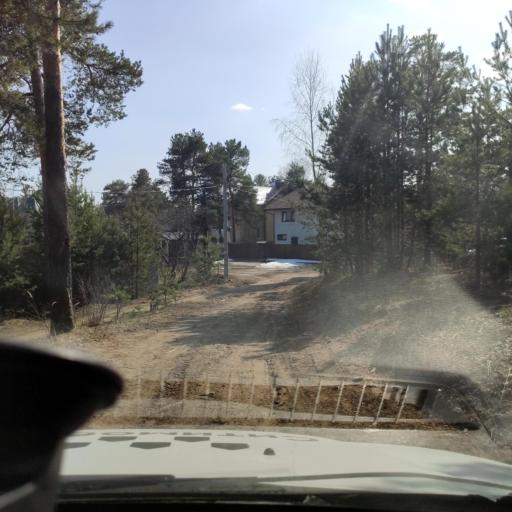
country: RU
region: Perm
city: Perm
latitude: 58.0554
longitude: 56.2891
